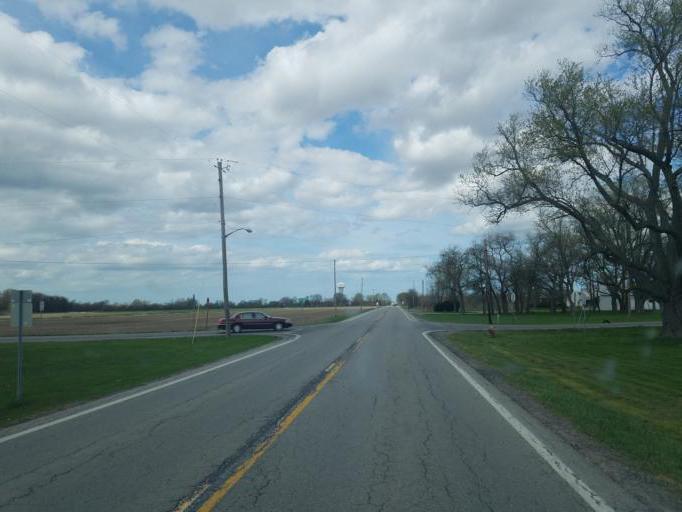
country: US
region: Ohio
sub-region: Huron County
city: Bellevue
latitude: 41.3244
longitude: -82.7669
